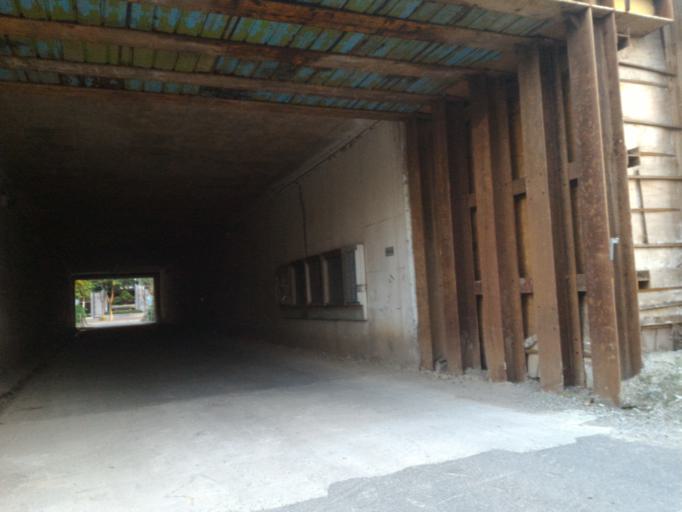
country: TW
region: Taiwan
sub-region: Taoyuan
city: Taoyuan
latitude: 24.9508
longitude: 121.3774
